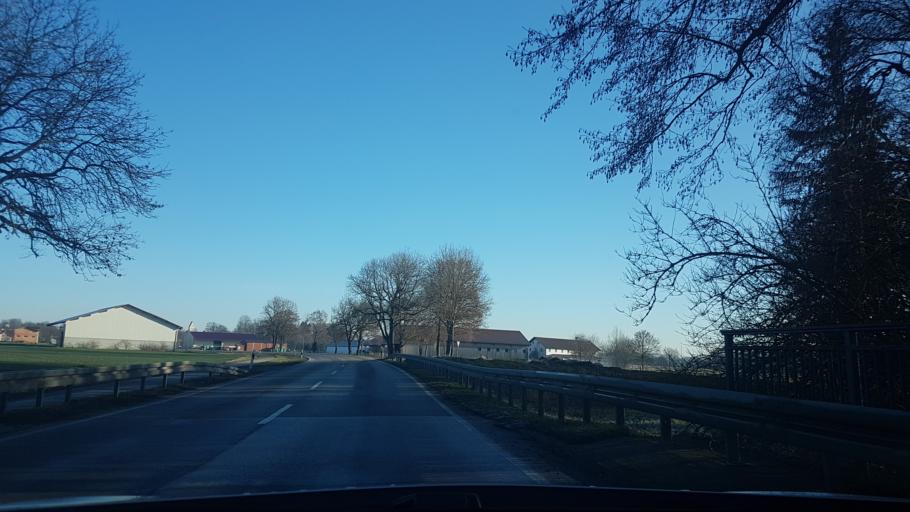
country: DE
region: Bavaria
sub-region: Upper Bavaria
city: Oberding
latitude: 48.3052
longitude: 11.8341
